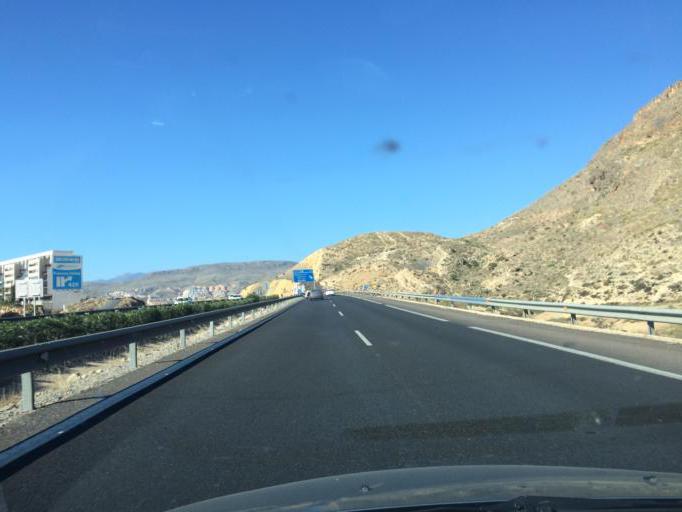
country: ES
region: Andalusia
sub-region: Provincia de Almeria
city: Aguadulce
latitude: 36.8261
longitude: -2.5815
